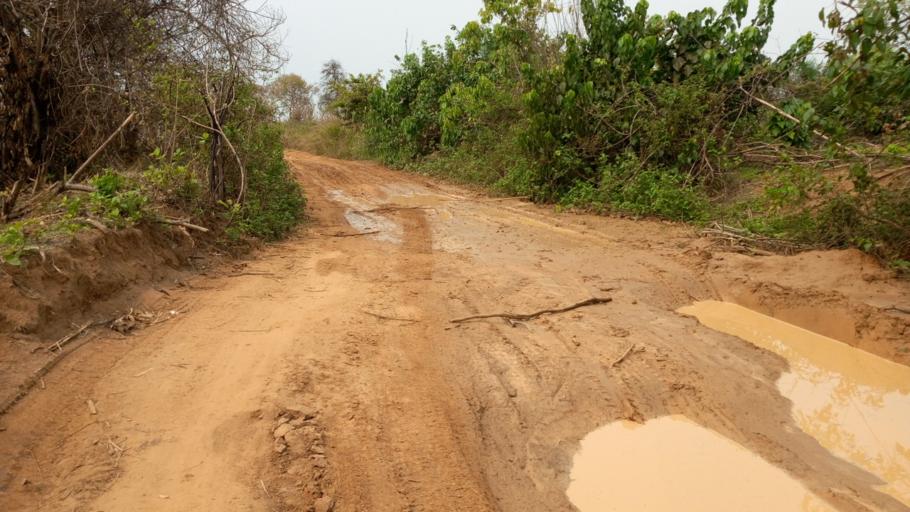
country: CD
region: Bandundu
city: Bandundu
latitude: -3.4565
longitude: 17.7689
